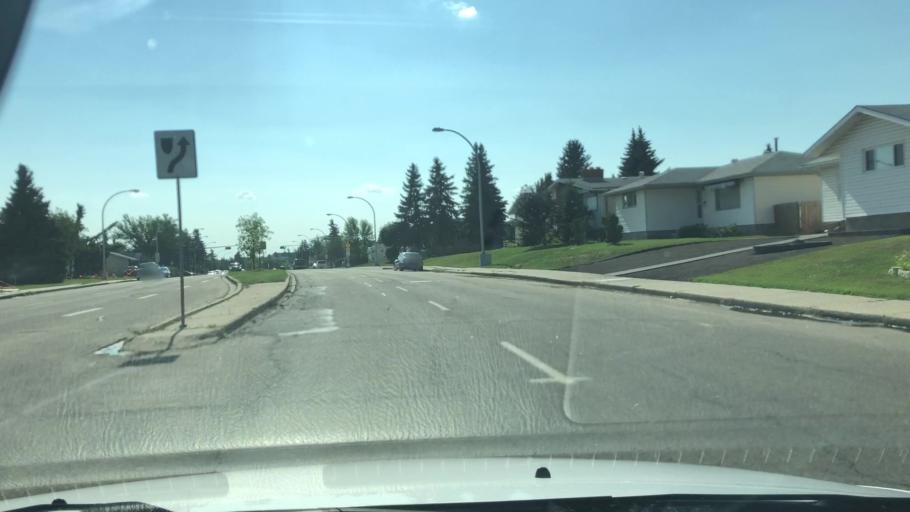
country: CA
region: Alberta
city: Edmonton
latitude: 53.6069
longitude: -113.4710
